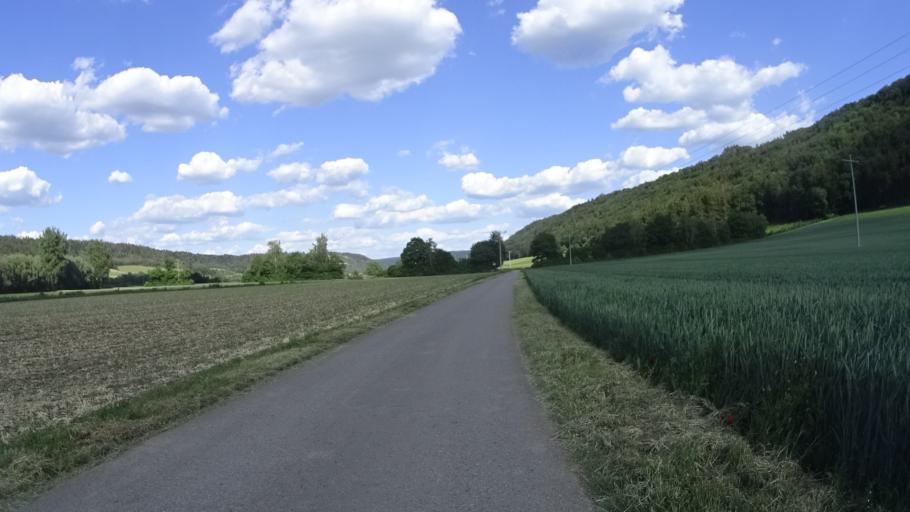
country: DE
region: Bavaria
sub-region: Upper Palatinate
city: Dietfurt
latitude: 49.0191
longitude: 11.4951
